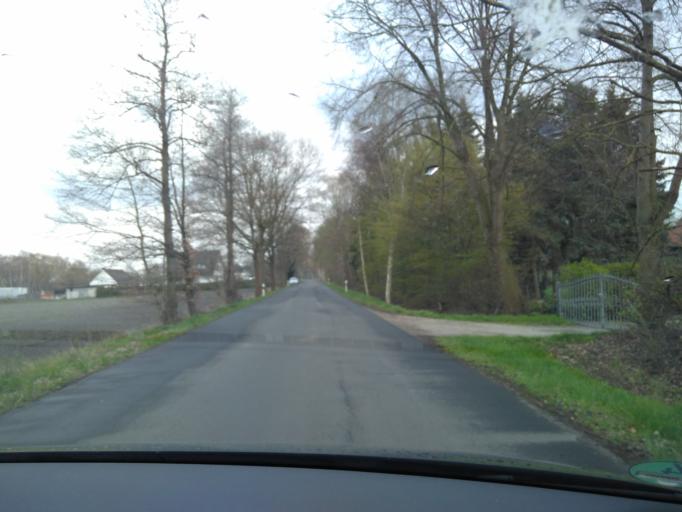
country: DE
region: Lower Saxony
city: Adelheidsdorf
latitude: 52.5524
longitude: 10.0020
